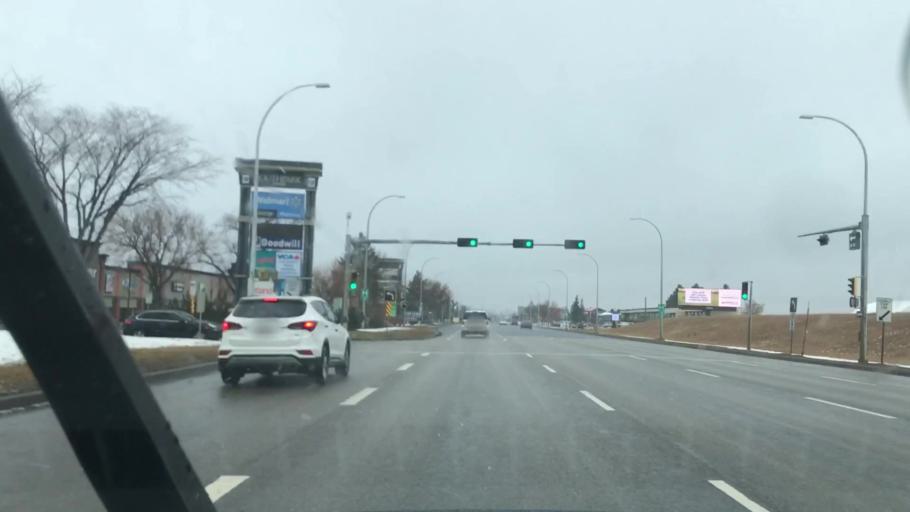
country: CA
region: Alberta
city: Edmonton
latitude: 53.4717
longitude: -113.4922
